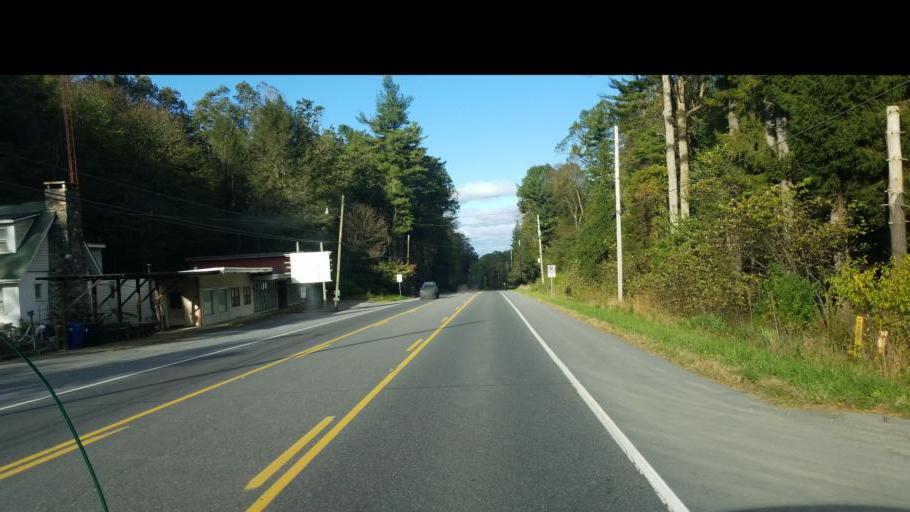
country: US
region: Pennsylvania
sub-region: Franklin County
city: Fayetteville
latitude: 39.8990
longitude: -77.4376
